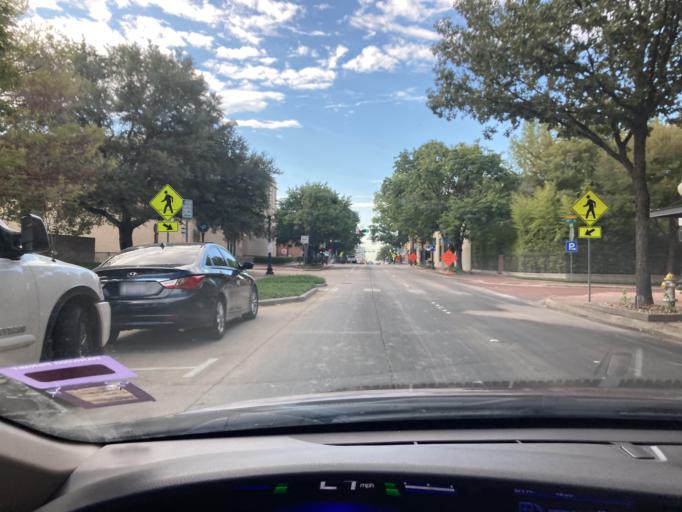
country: US
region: Texas
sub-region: Collin County
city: Plano
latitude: 33.0205
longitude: -96.6992
